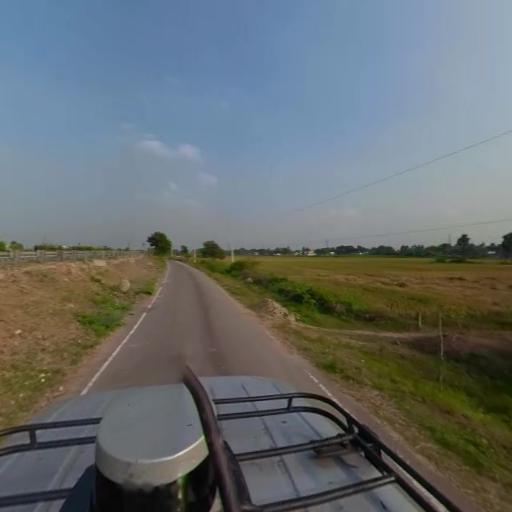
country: IN
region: Telangana
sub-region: Nalgonda
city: Suriapet
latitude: 17.1646
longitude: 79.5215
